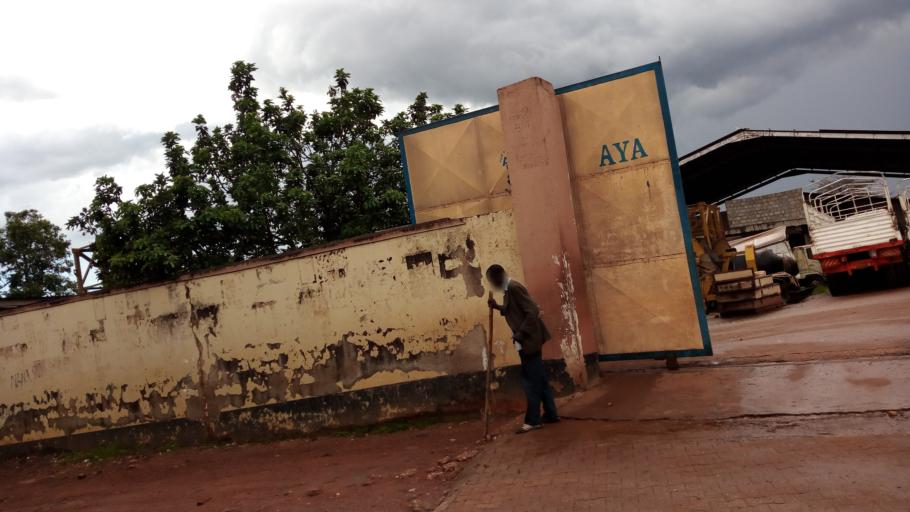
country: UG
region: Central Region
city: Kampala Central Division
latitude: 0.3772
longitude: 32.5557
